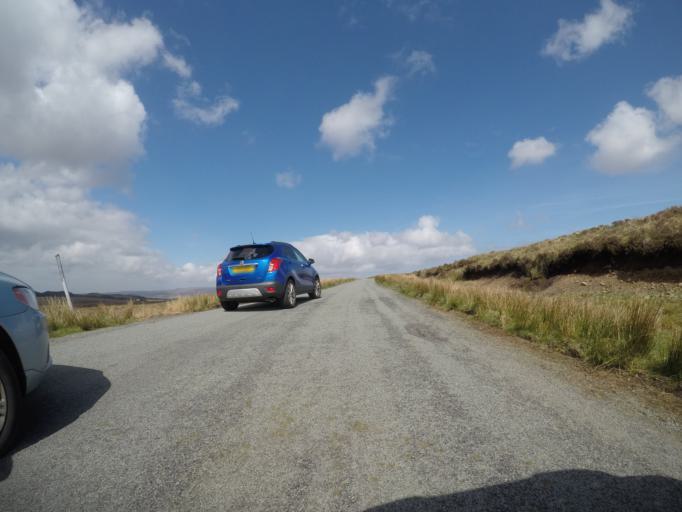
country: GB
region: Scotland
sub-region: Highland
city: Isle of Skye
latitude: 57.4177
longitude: -6.2935
